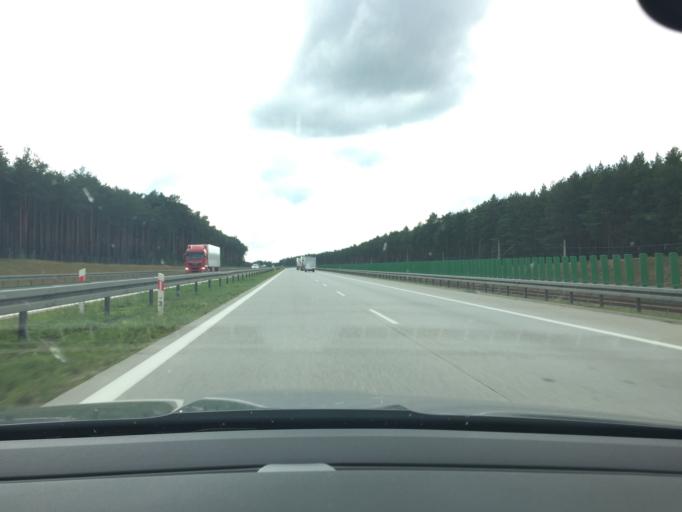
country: PL
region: Lubusz
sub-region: Powiat slubicki
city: Rzepin
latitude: 52.3333
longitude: 14.8146
